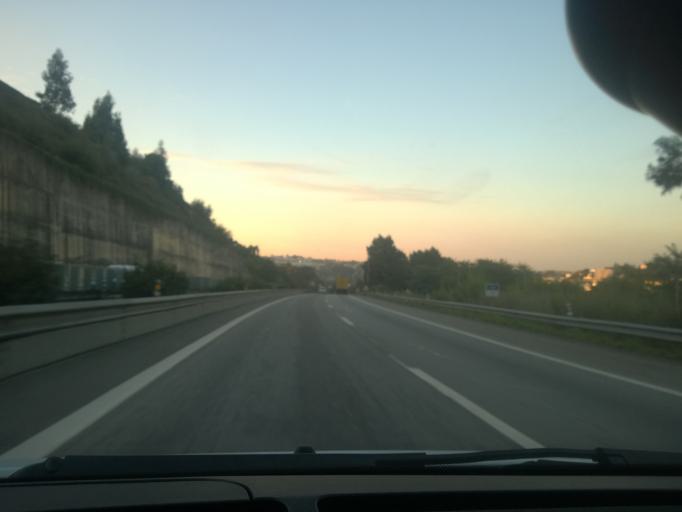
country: PT
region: Porto
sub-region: Vila Nova de Gaia
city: Oliveira do Douro
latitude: 41.1298
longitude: -8.5759
